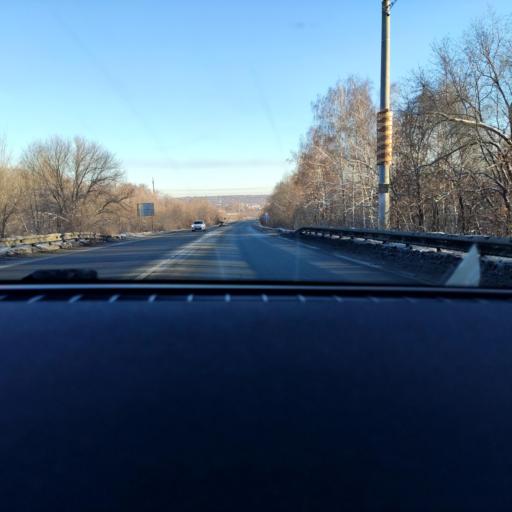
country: RU
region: Samara
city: Novokuybyshevsk
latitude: 53.0737
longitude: 50.0008
